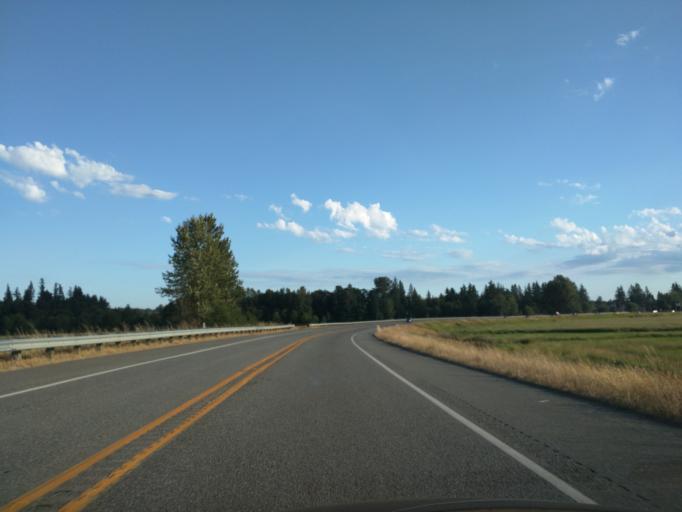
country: US
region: Washington
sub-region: Snohomish County
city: Arlington
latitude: 48.1929
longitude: -122.1391
